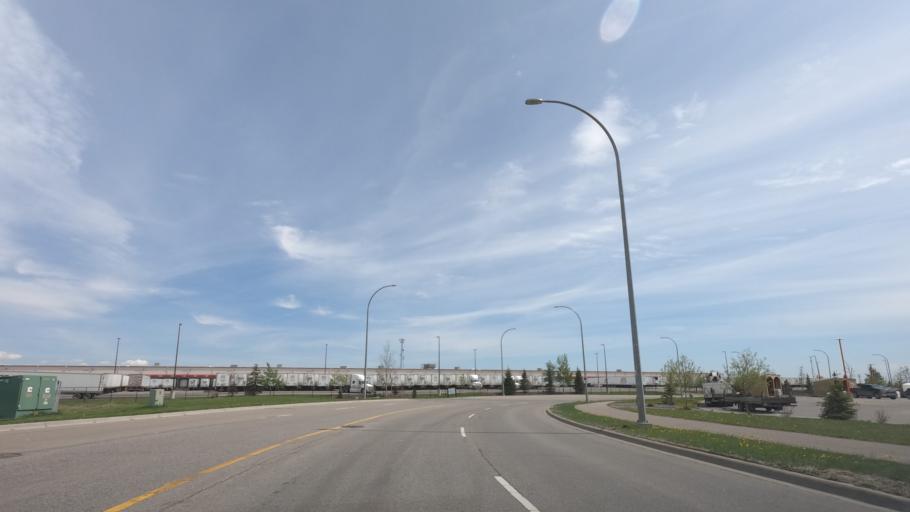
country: CA
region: Alberta
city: Airdrie
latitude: 51.3042
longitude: -113.9960
